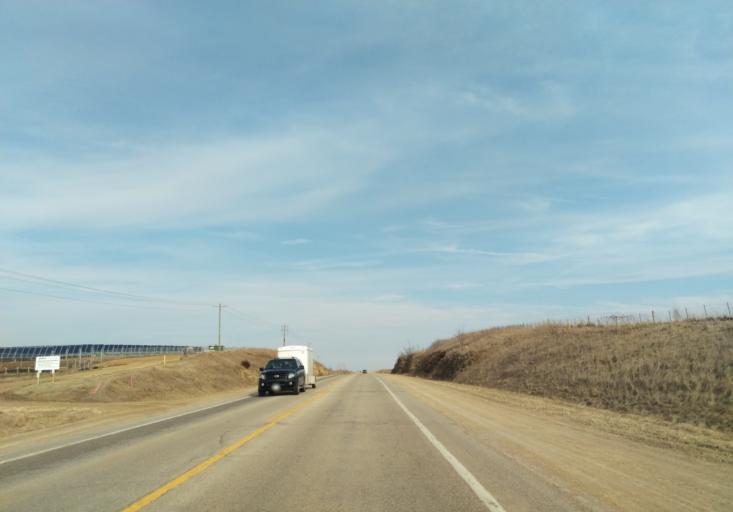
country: US
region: Wisconsin
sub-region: Grant County
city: Lancaster
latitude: 42.9741
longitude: -90.8321
